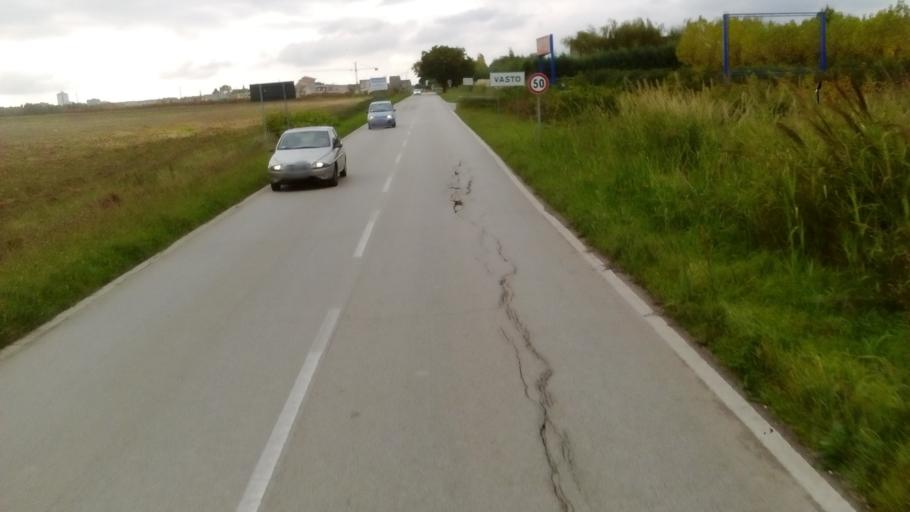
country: IT
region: Abruzzo
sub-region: Provincia di Chieti
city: Vasto
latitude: 42.1514
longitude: 14.6994
